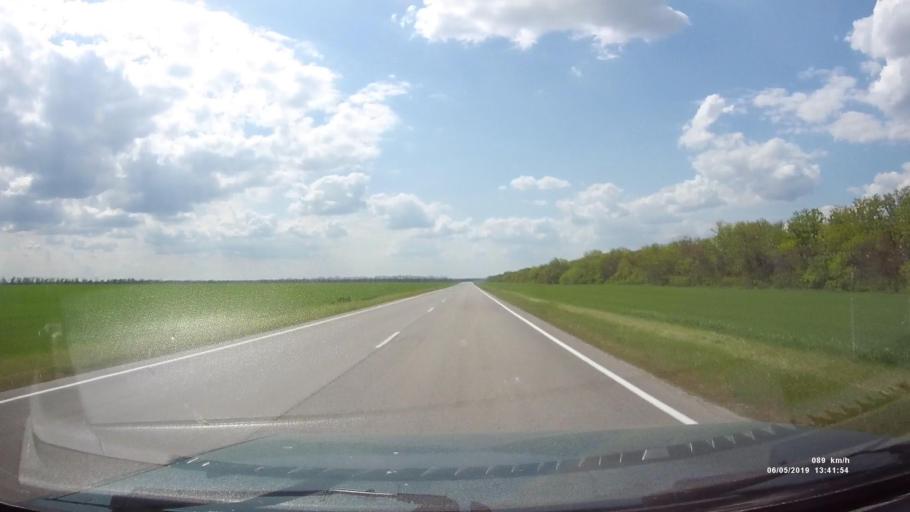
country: RU
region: Rostov
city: Semikarakorsk
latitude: 47.6613
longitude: 40.6674
